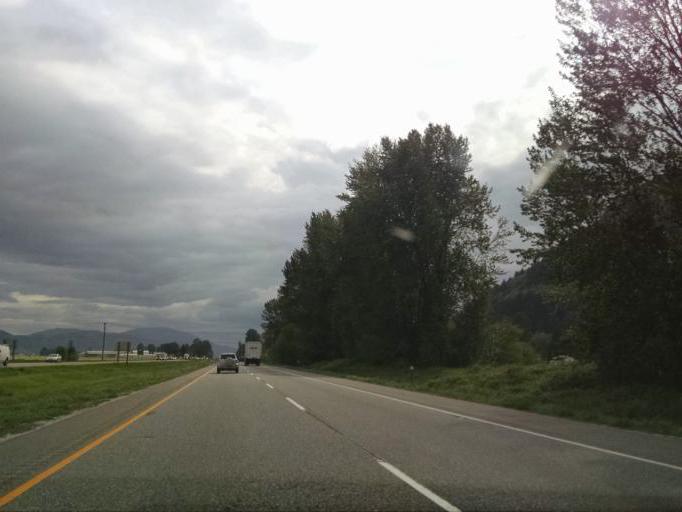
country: CA
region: British Columbia
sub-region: Fraser Valley Regional District
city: Chilliwack
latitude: 49.1182
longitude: -122.1031
